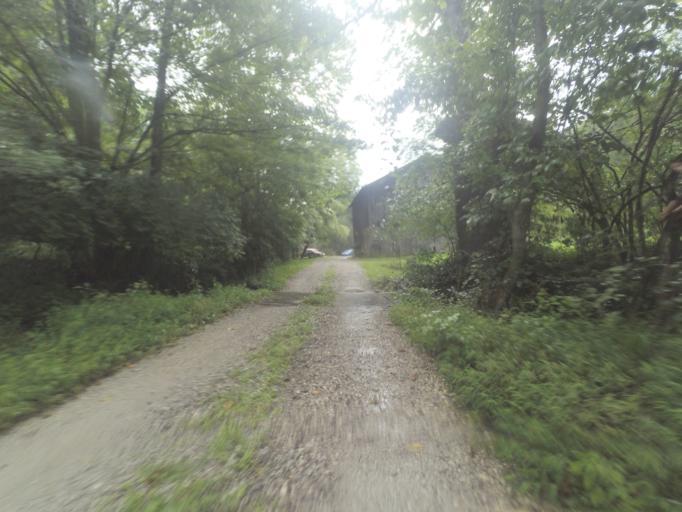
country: US
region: West Virginia
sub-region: Cabell County
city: Huntington
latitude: 38.3780
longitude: -82.3946
